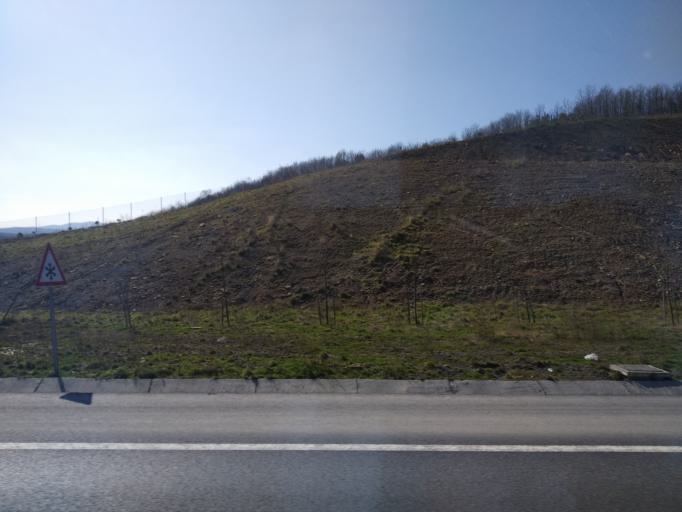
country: TR
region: Istanbul
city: Mahmut Sevket Pasa
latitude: 41.1565
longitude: 29.2650
